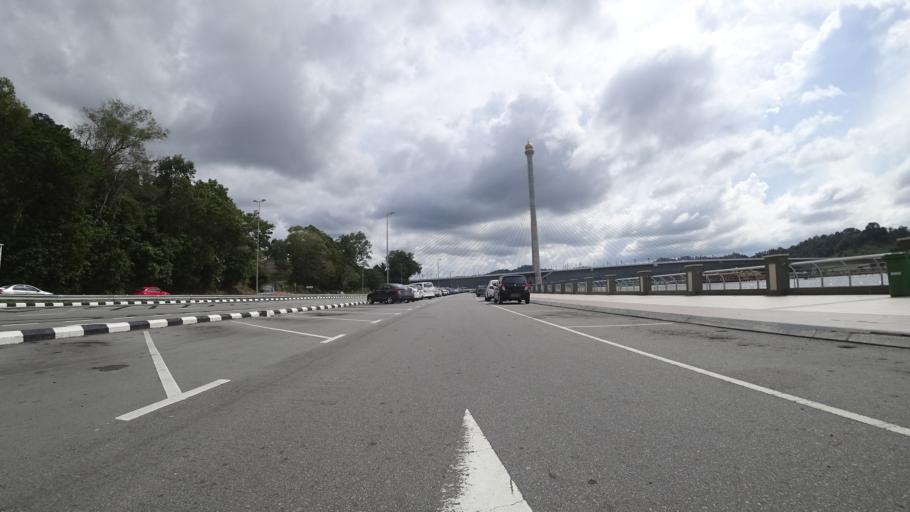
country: BN
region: Brunei and Muara
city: Bandar Seri Begawan
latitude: 4.8797
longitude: 114.9506
